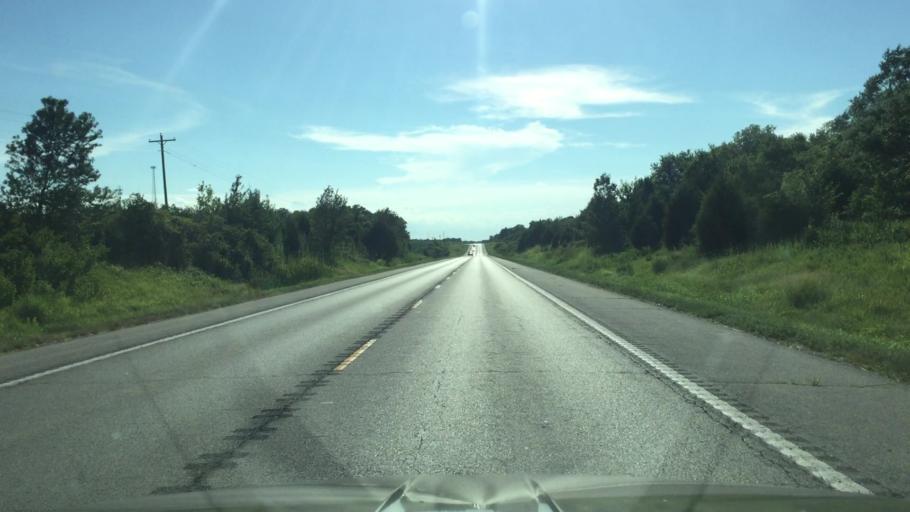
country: US
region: Missouri
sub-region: Pettis County
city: Sedalia
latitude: 38.6934
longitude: -93.0877
